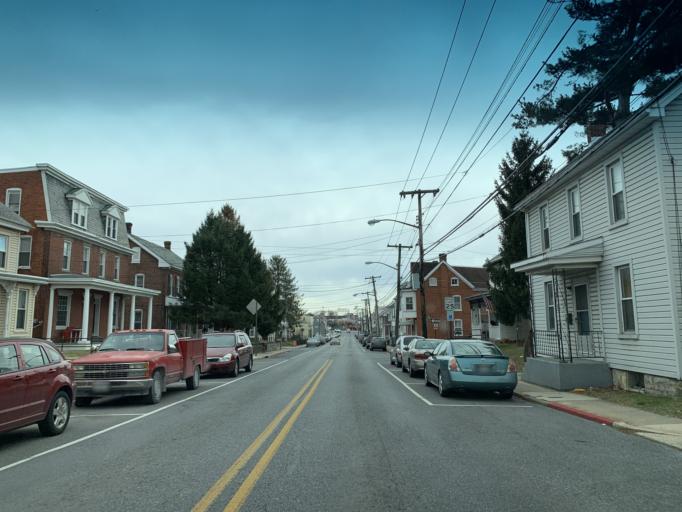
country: US
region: Maryland
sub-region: Washington County
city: Hagerstown
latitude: 39.6503
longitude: -77.7271
